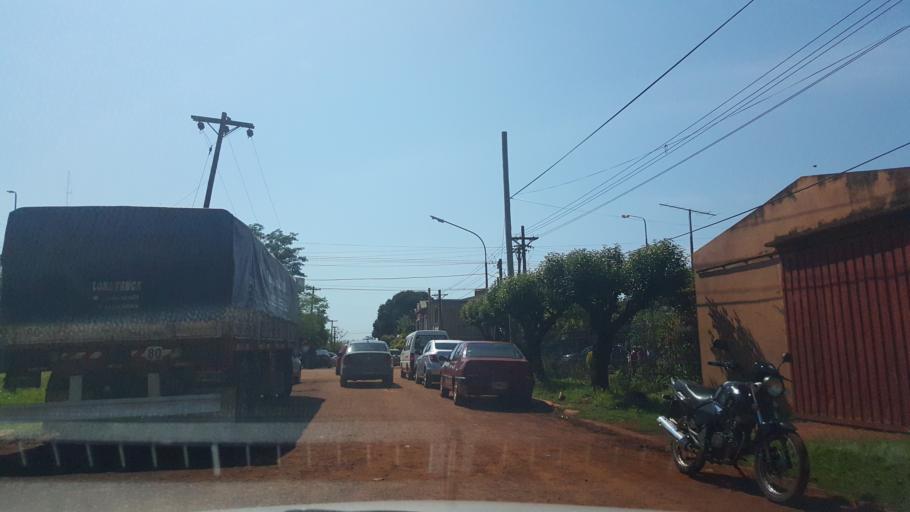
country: AR
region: Corrientes
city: San Carlos
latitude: -27.7452
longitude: -55.8993
